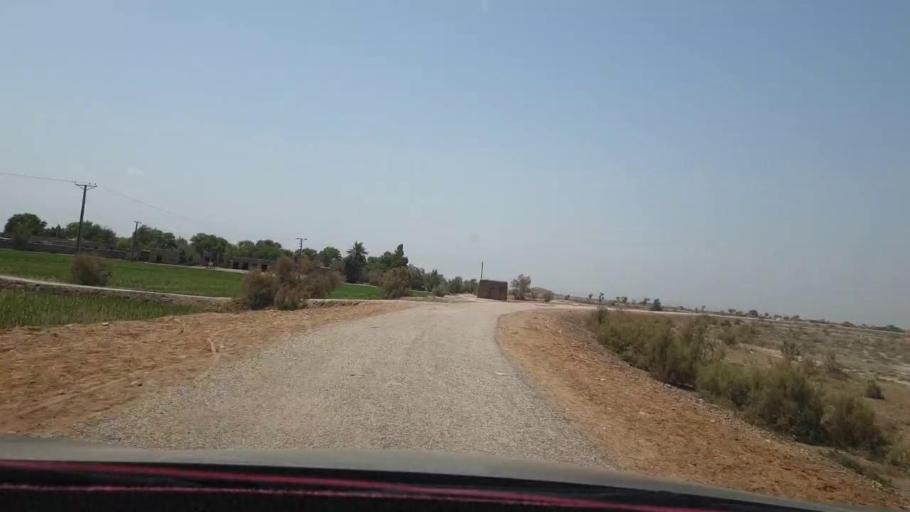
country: PK
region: Sindh
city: Warah
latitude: 27.5044
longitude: 67.7080
